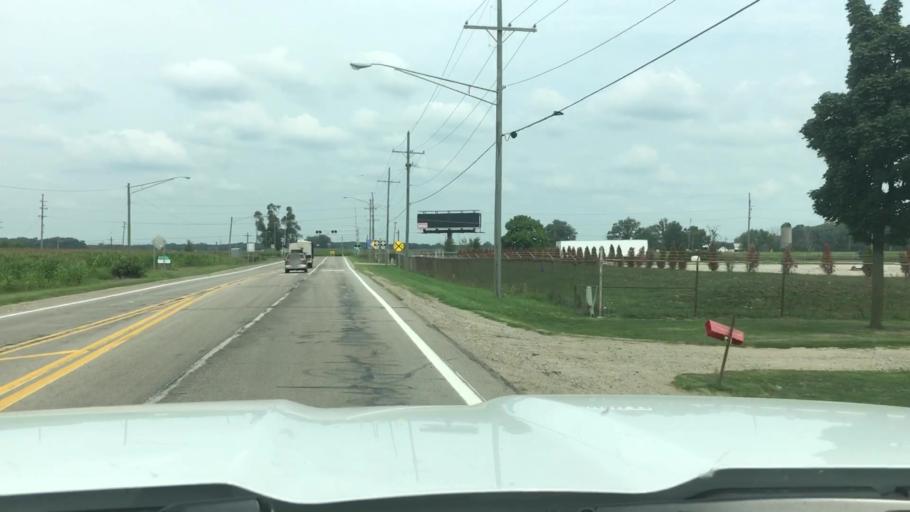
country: US
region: Michigan
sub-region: Ingham County
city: Webberville
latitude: 42.6664
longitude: -84.1985
